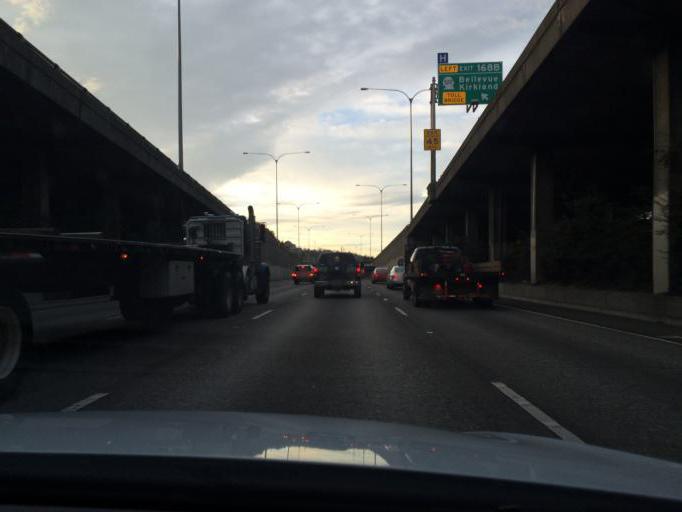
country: US
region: Washington
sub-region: King County
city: Seattle
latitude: 47.6469
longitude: -122.3227
